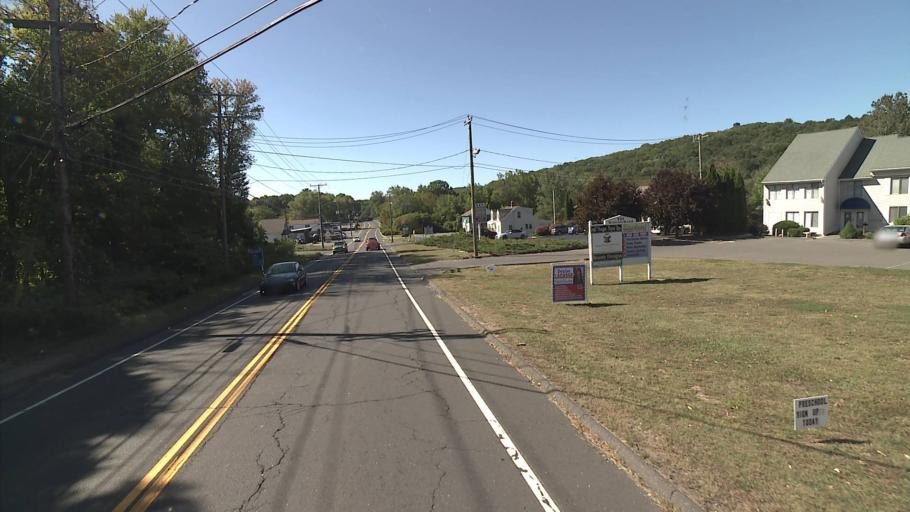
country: US
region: Connecticut
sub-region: New Haven County
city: Wolcott
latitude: 41.5899
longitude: -72.9910
